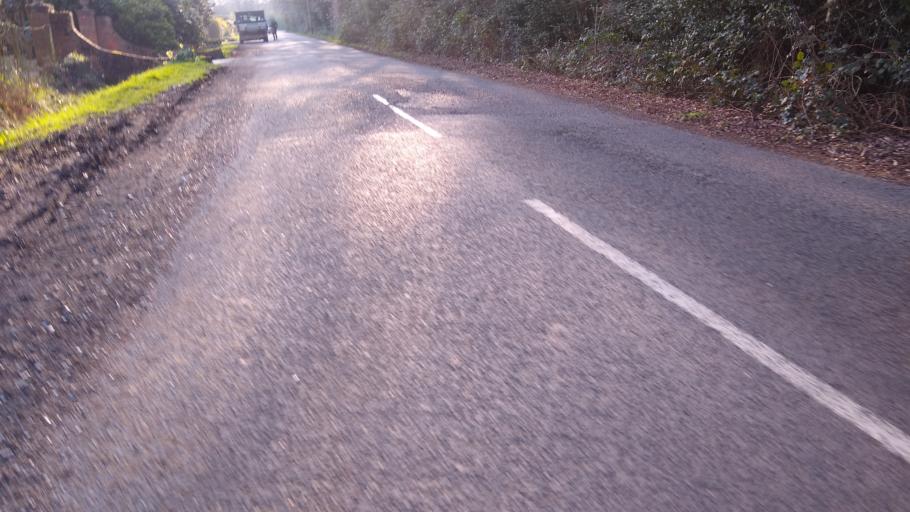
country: GB
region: England
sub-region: Wokingham
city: Twyford
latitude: 51.4536
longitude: -0.8615
